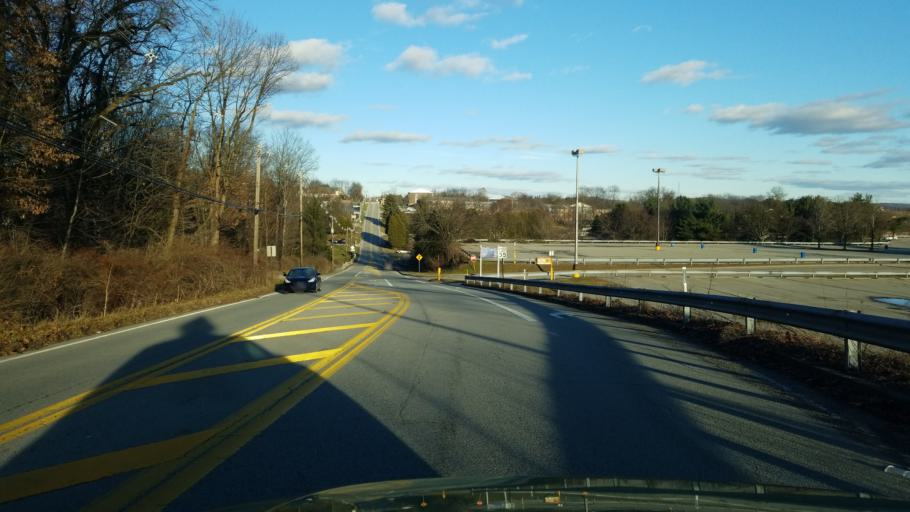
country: US
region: Pennsylvania
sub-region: Indiana County
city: Indiana
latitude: 40.6103
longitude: -79.1862
